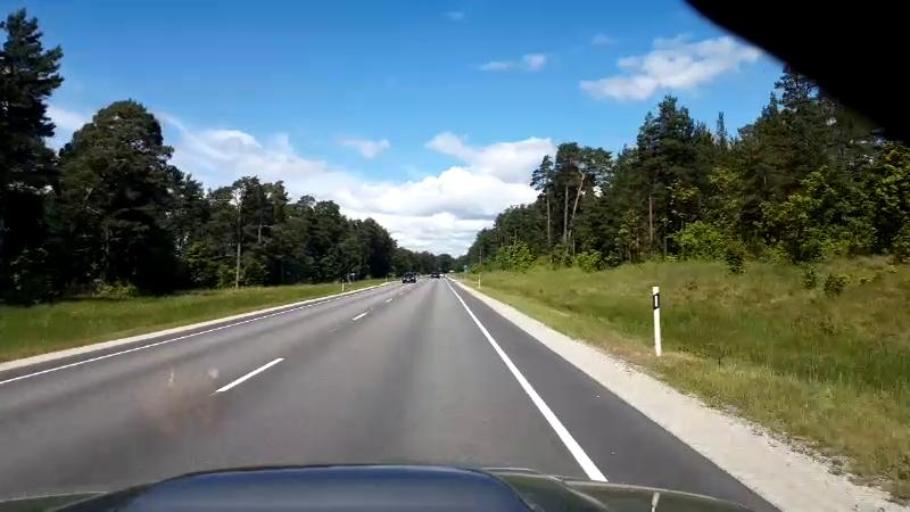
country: EE
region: Paernumaa
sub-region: Paernu linn
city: Parnu
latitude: 58.1985
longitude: 24.4868
